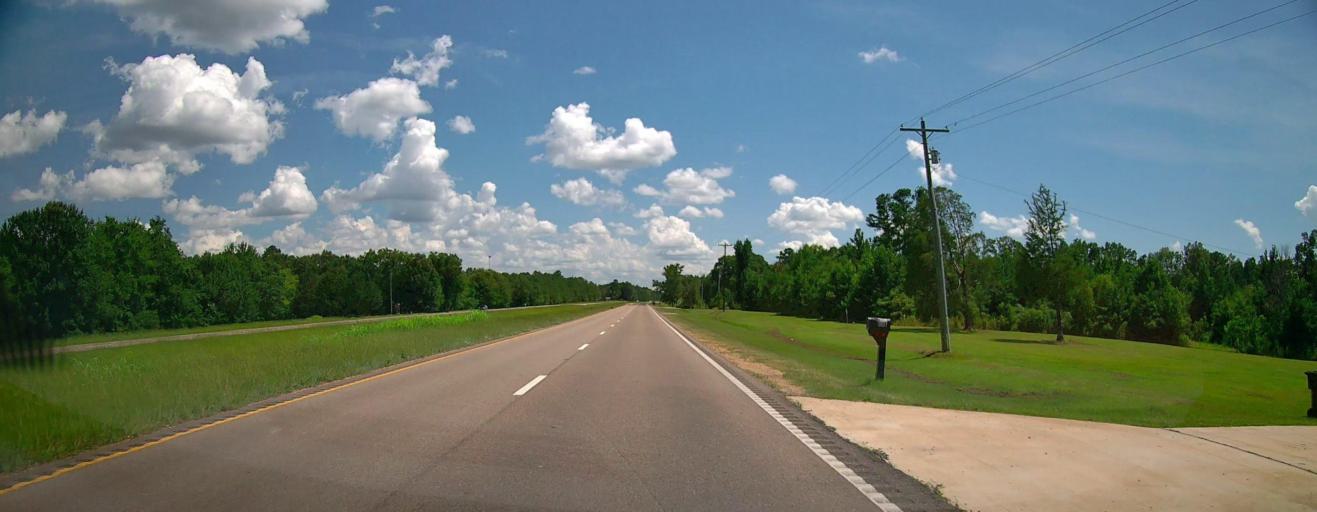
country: US
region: Mississippi
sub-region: Monroe County
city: Amory
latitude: 33.9339
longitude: -88.5970
